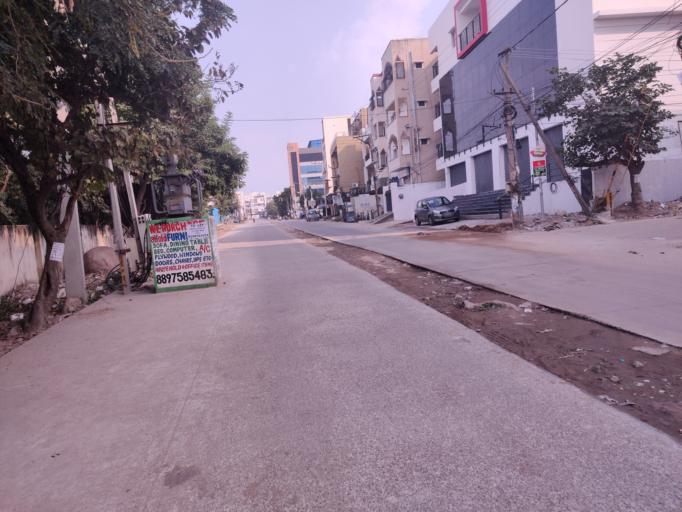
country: IN
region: Telangana
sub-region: Hyderabad
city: Hyderabad
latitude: 17.4035
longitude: 78.3878
